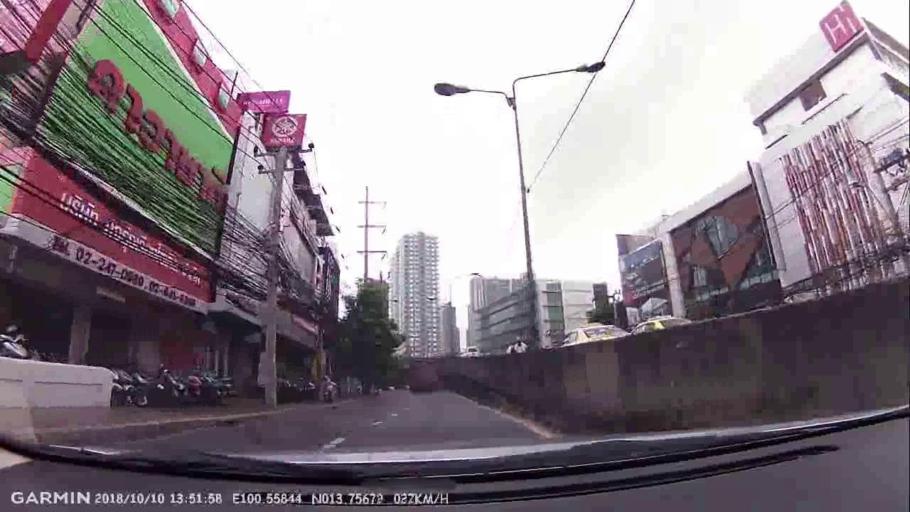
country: TH
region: Bangkok
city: Din Daeng
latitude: 13.7568
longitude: 100.5585
